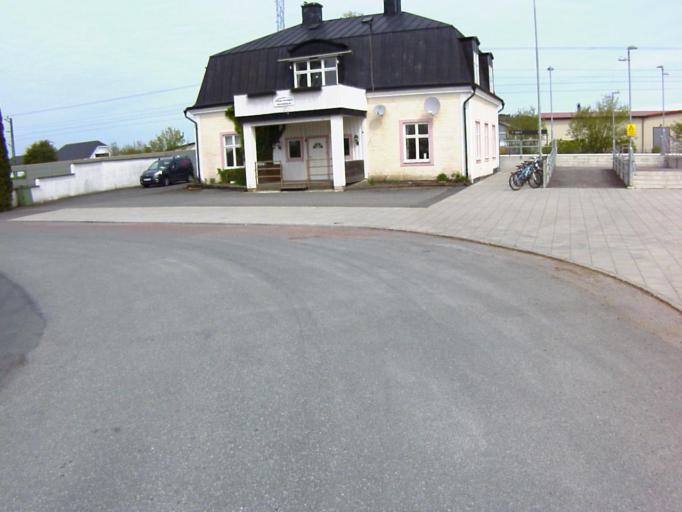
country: SE
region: Skane
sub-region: Kristianstads Kommun
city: Fjalkinge
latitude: 56.0434
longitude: 14.2794
